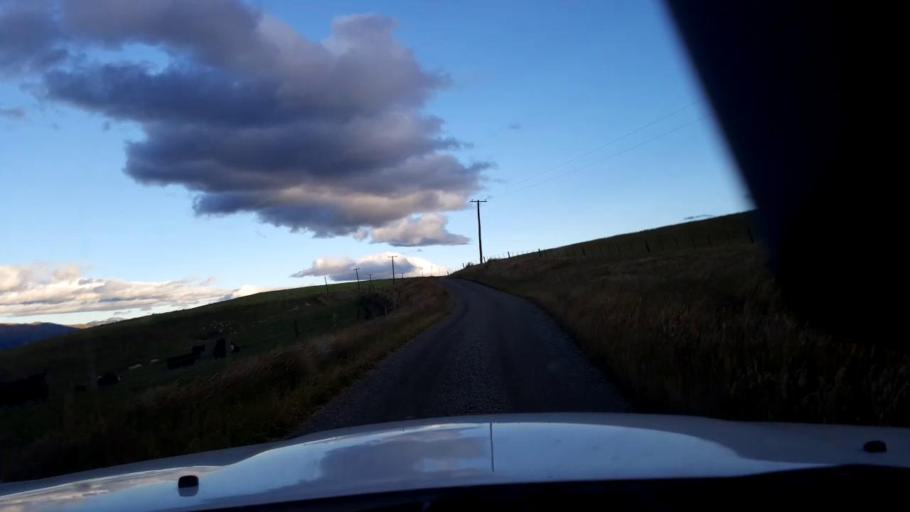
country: NZ
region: Canterbury
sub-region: Timaru District
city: Pleasant Point
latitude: -44.2537
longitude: 170.9111
